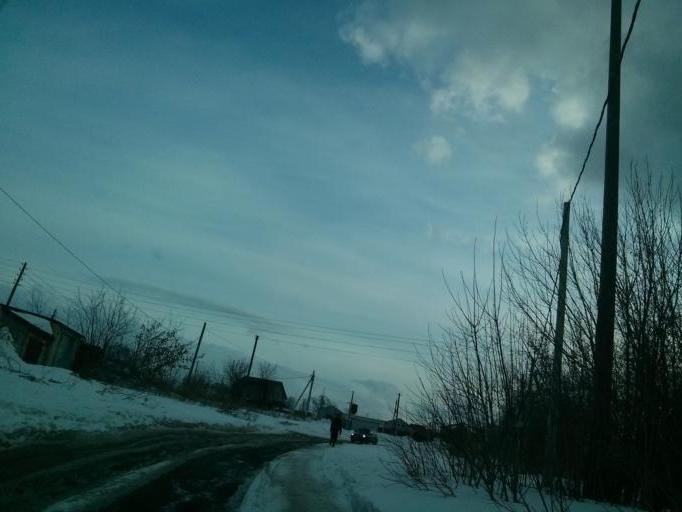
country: RU
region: Nizjnij Novgorod
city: Afonino
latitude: 56.2723
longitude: 44.0331
